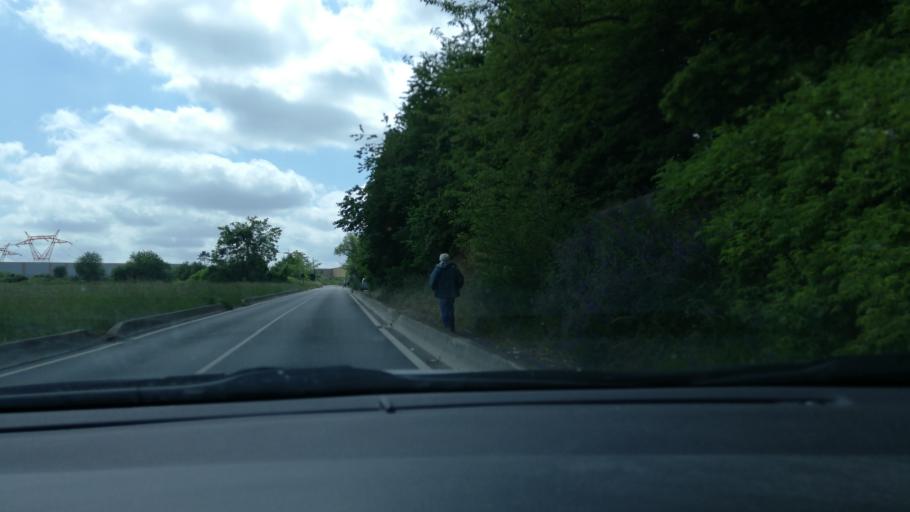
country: FR
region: Ile-de-France
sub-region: Departement du Val-d'Oise
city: Vaureal
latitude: 49.0682
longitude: 2.0250
